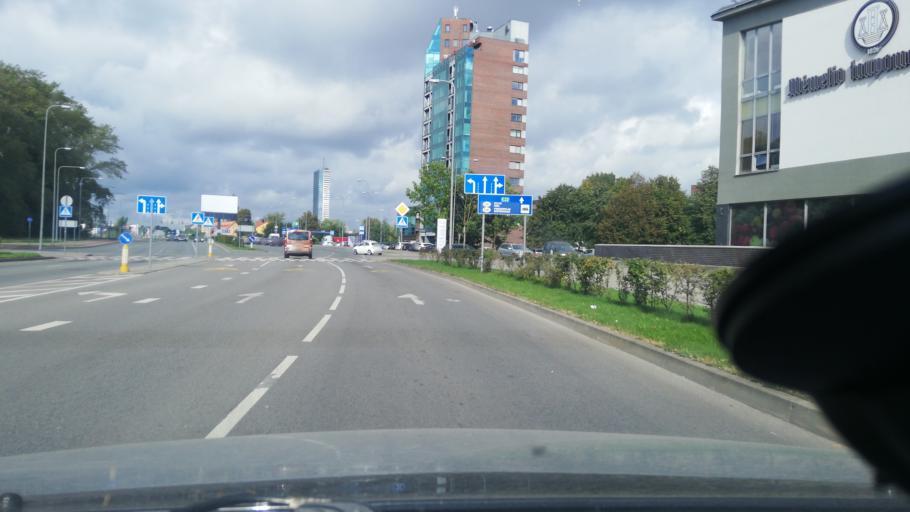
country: LT
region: Klaipedos apskritis
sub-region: Klaipeda
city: Klaipeda
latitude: 55.6818
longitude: 21.1507
